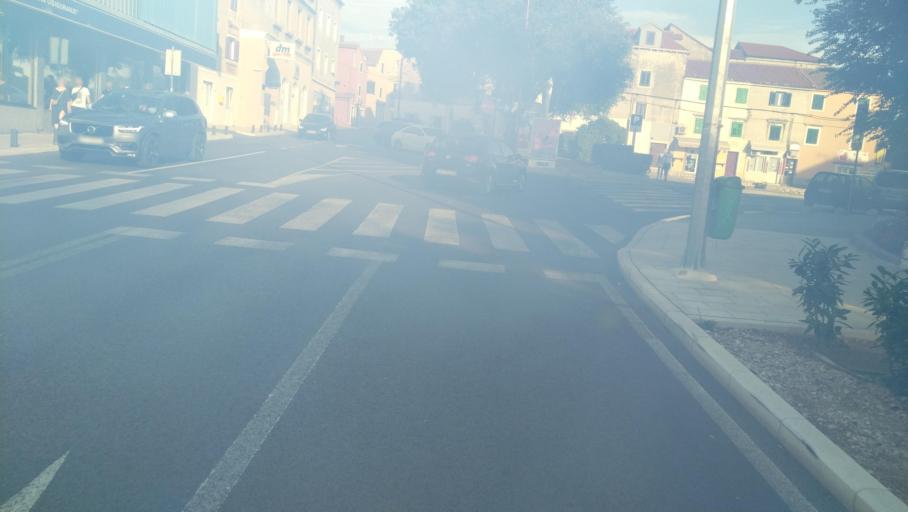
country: HR
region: Sibensko-Kniniska
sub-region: Grad Sibenik
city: Sibenik
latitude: 43.7341
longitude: 15.8949
